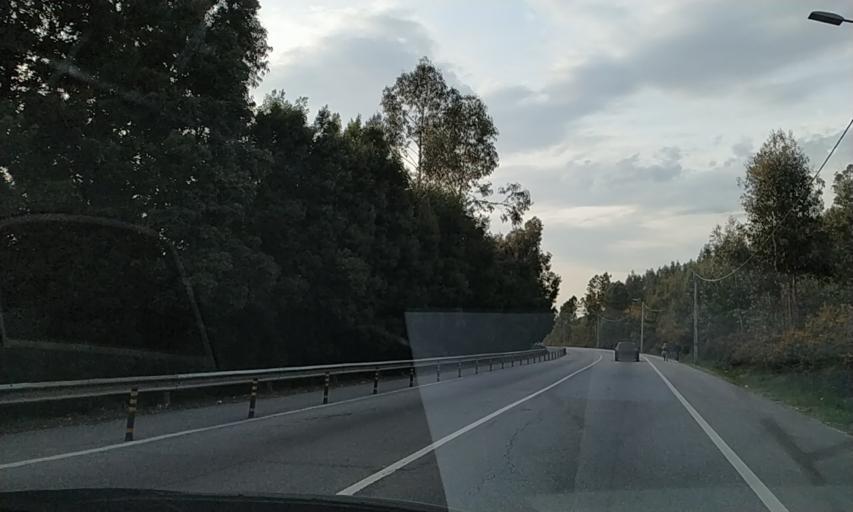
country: PT
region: Porto
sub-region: Valongo
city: Valongo
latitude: 41.1982
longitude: -8.5233
